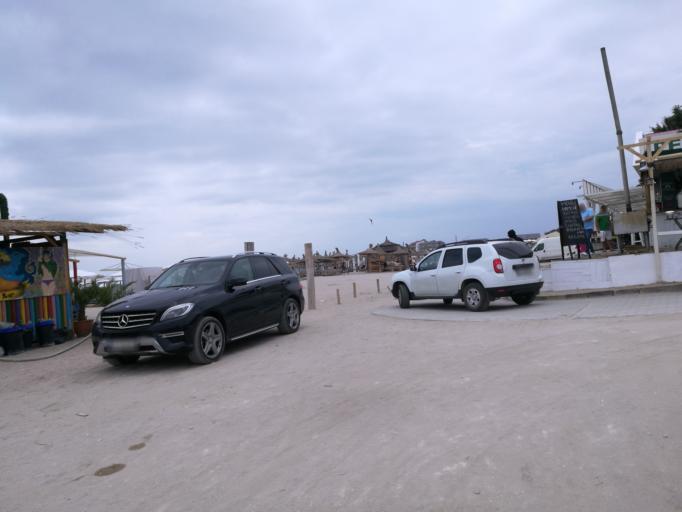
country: RO
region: Constanta
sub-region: Municipiul Mangalia
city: Mangalia
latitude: 43.7550
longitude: 28.5742
